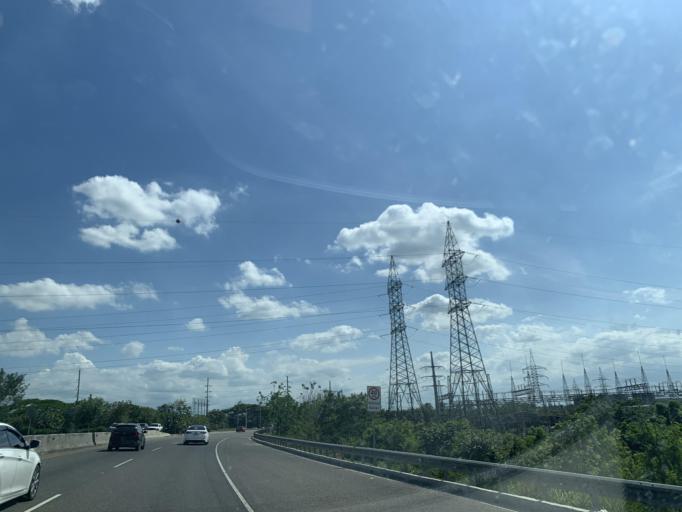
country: DO
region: Santiago
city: Licey al Medio
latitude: 19.4159
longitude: -70.6418
